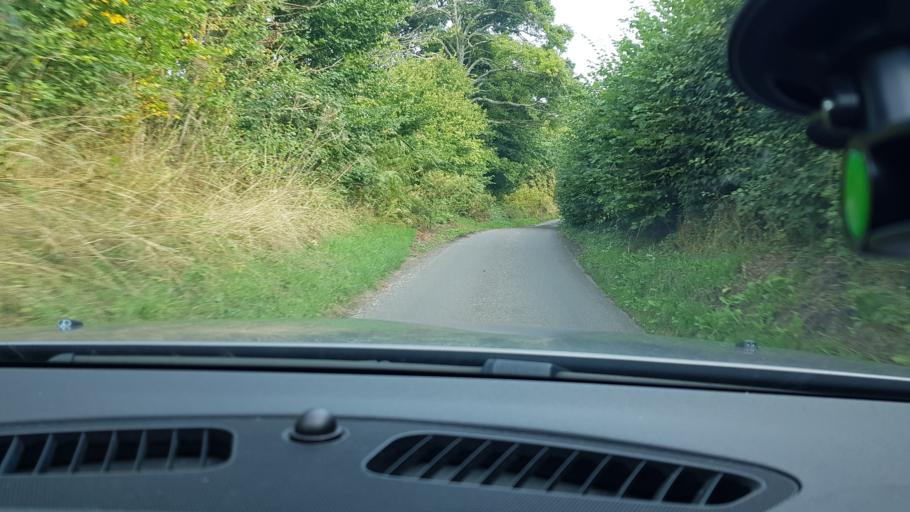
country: GB
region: England
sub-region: Wiltshire
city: Chilton Foliat
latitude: 51.4439
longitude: -1.5564
